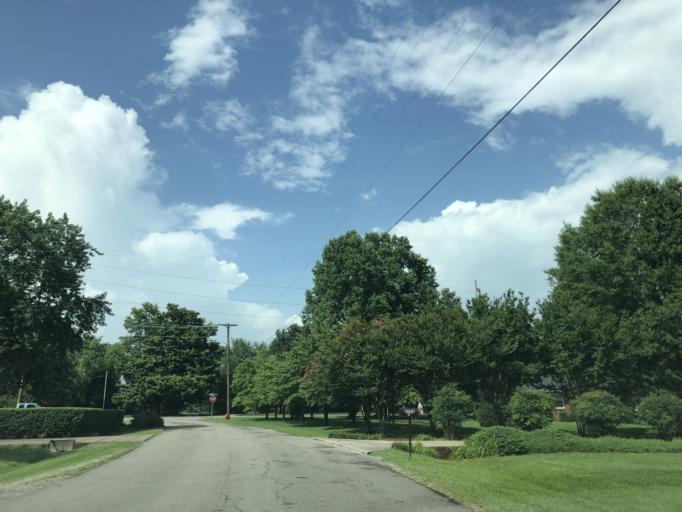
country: US
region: Tennessee
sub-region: Davidson County
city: Lakewood
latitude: 36.1847
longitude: -86.6742
